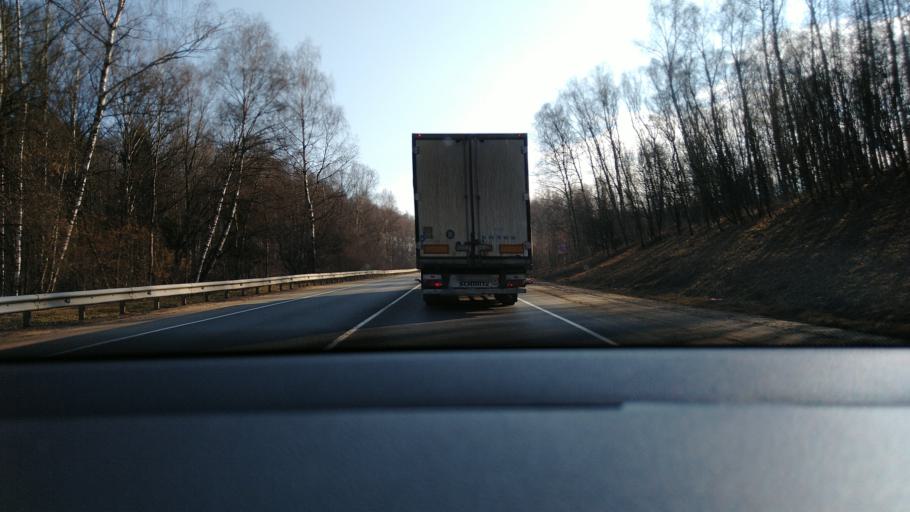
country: RU
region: Moskovskaya
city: Dubrovitsy
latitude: 55.3733
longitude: 37.4106
